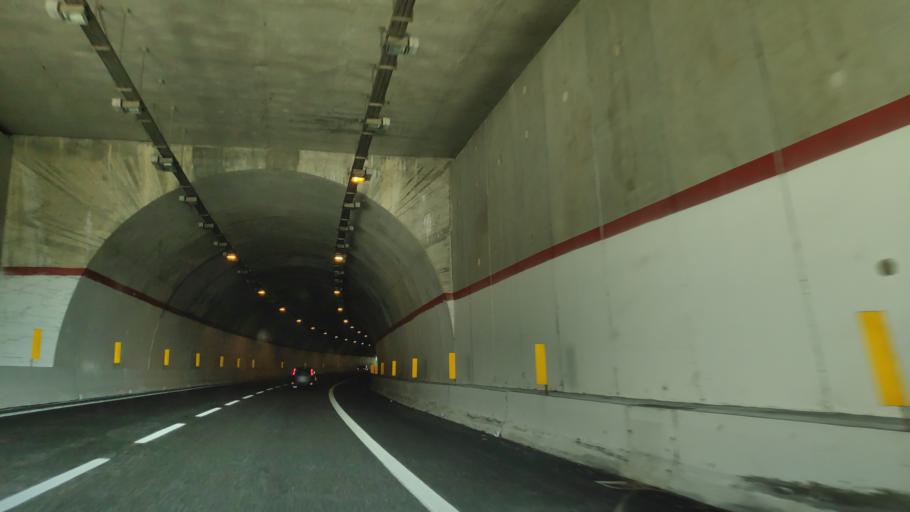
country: IT
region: Basilicate
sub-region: Provincia di Potenza
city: Lauria
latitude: 40.0217
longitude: 15.8802
